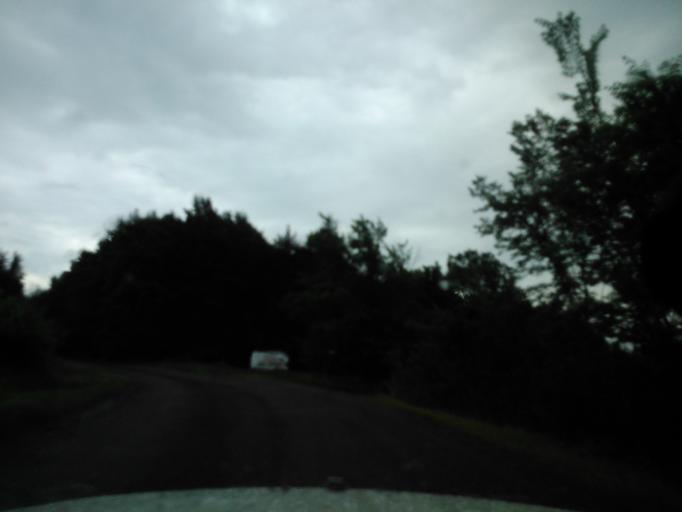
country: PL
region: Pomeranian Voivodeship
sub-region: Powiat slupski
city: Smoldzino
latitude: 54.6570
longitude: 17.2233
